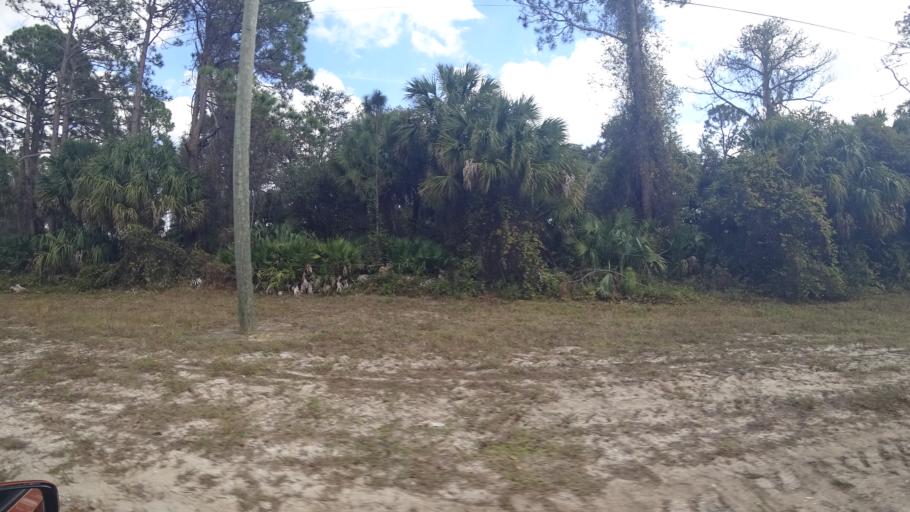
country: US
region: Florida
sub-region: Charlotte County
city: Port Charlotte
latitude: 27.0359
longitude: -82.1336
